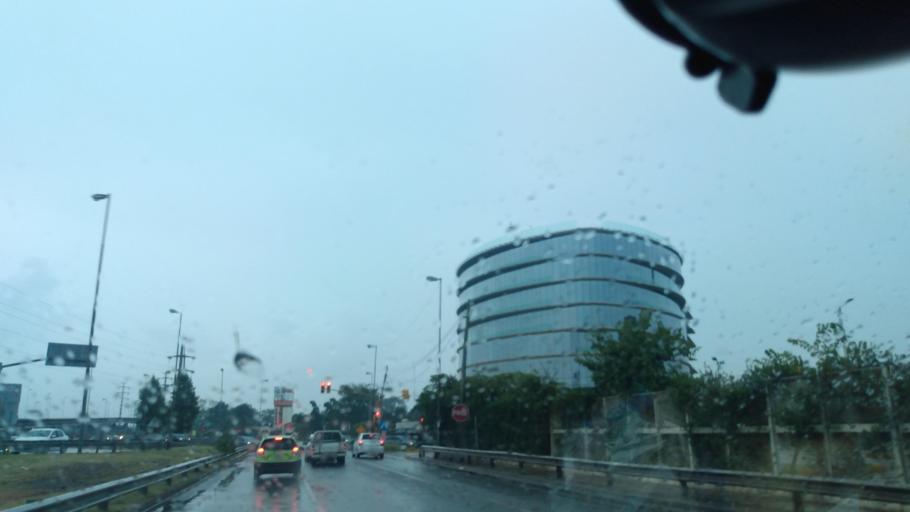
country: AR
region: Buenos Aires
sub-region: Partido de Tigre
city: Tigre
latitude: -34.4864
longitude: -58.5928
